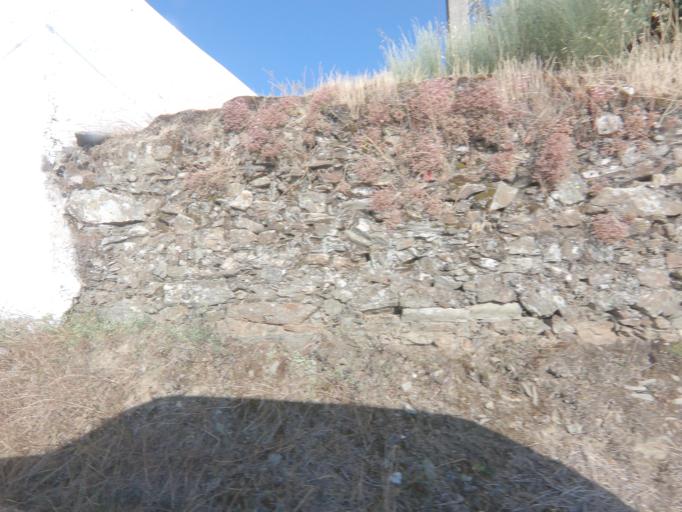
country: PT
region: Vila Real
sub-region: Sabrosa
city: Vilela
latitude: 41.1944
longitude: -7.6194
